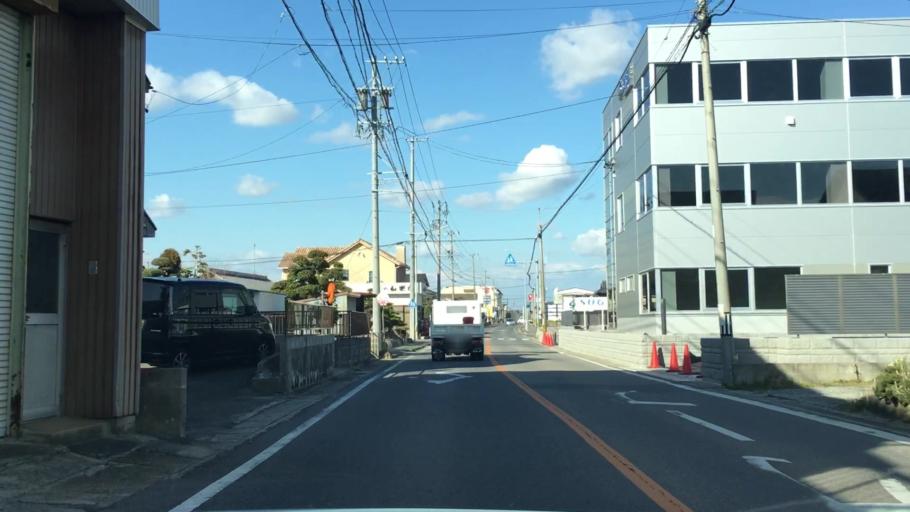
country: JP
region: Aichi
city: Nishio
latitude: 34.8307
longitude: 137.0409
